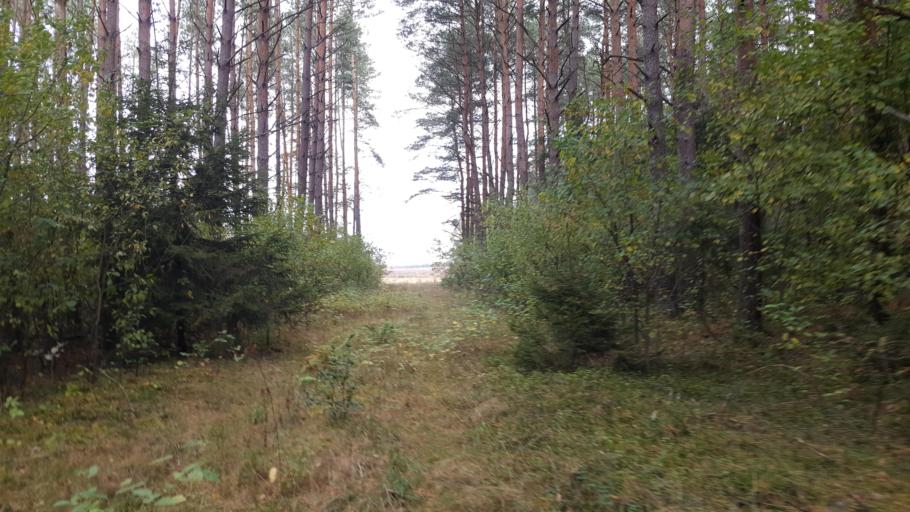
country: BY
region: Brest
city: Kamyanyets
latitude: 52.4269
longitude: 23.9034
